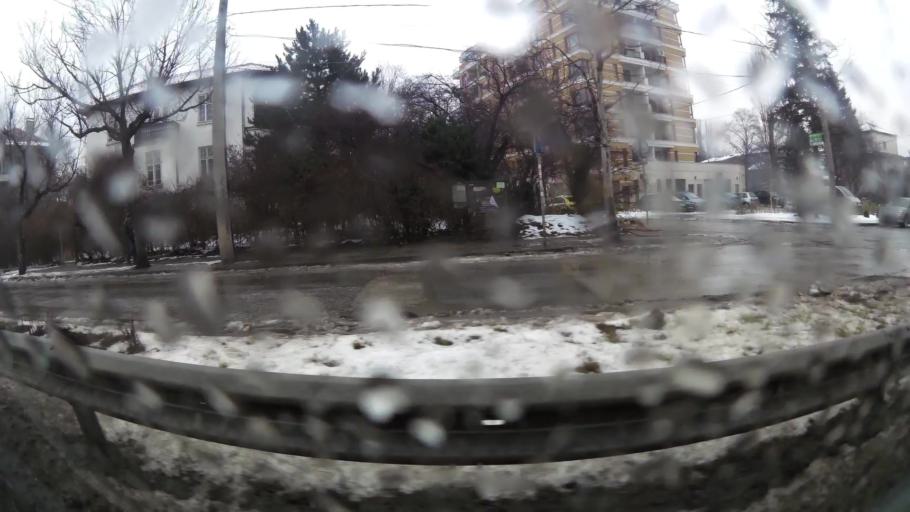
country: BG
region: Sofia-Capital
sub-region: Stolichna Obshtina
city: Sofia
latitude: 42.6672
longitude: 23.2575
